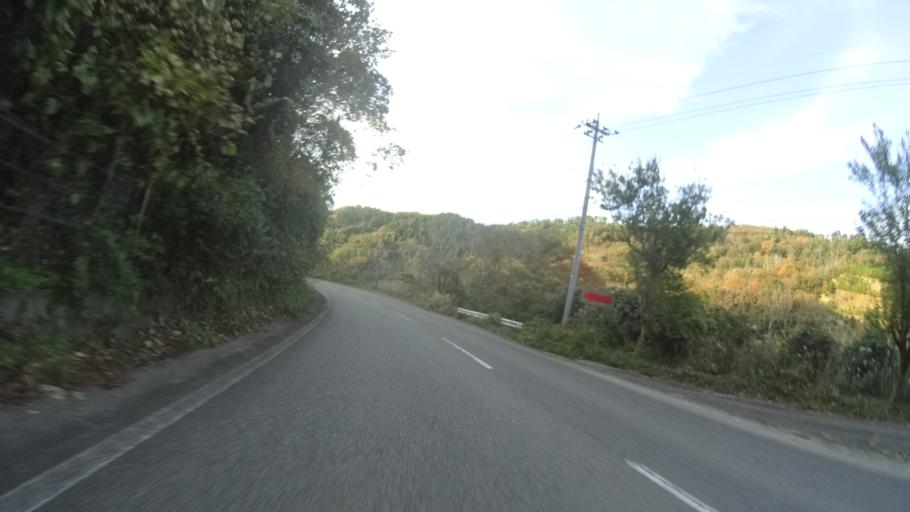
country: JP
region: Ishikawa
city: Nanao
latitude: 37.2154
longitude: 136.7064
